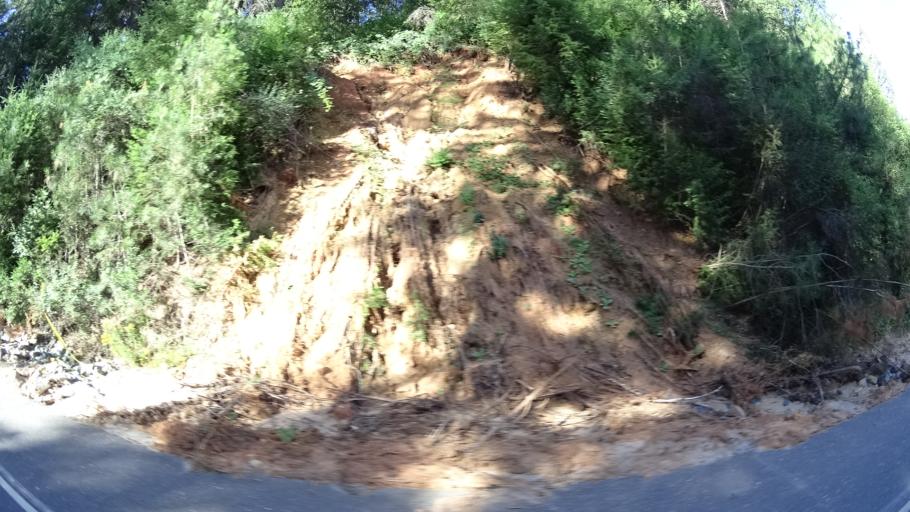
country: US
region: California
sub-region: Amador County
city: Pioneer
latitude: 38.3886
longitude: -120.5259
